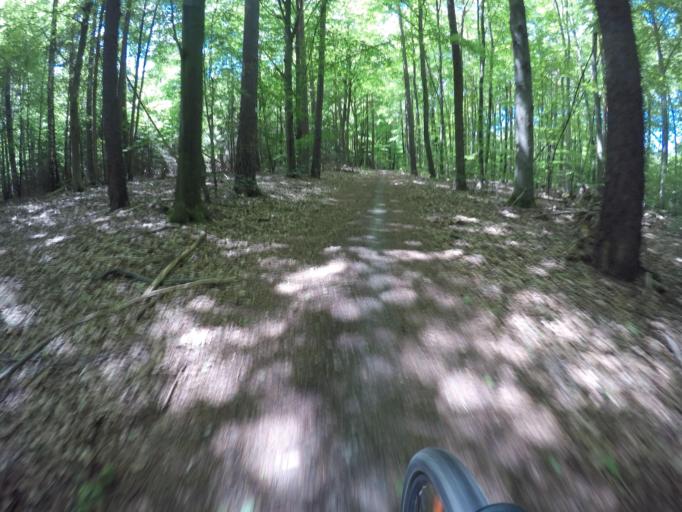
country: DE
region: Baden-Wuerttemberg
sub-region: Regierungsbezirk Stuttgart
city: Sindelfingen
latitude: 48.7385
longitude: 9.0490
